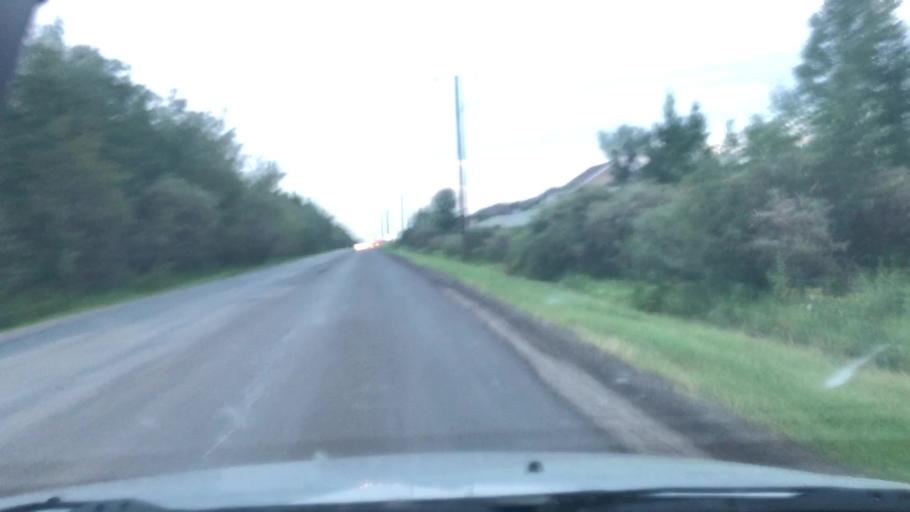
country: CA
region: Alberta
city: Devon
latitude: 53.4932
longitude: -113.6889
